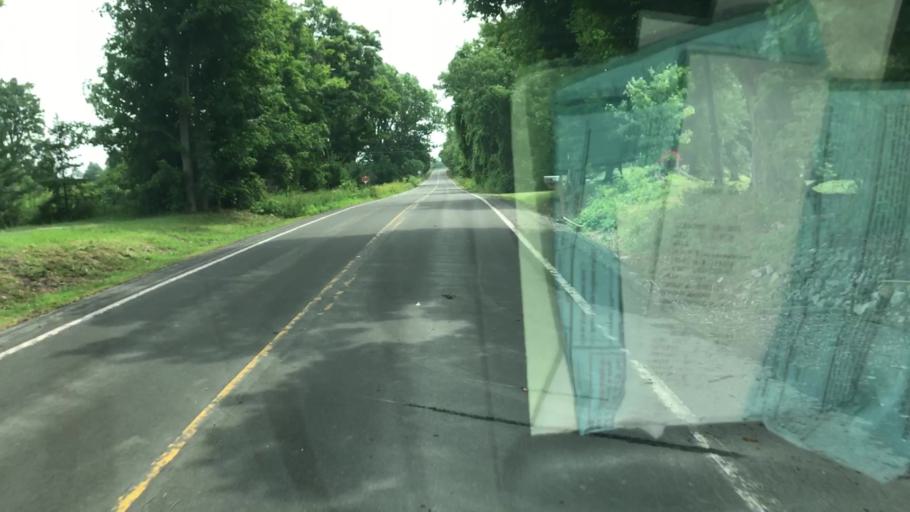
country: US
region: New York
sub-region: Onondaga County
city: Manlius
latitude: 42.9425
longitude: -75.9792
